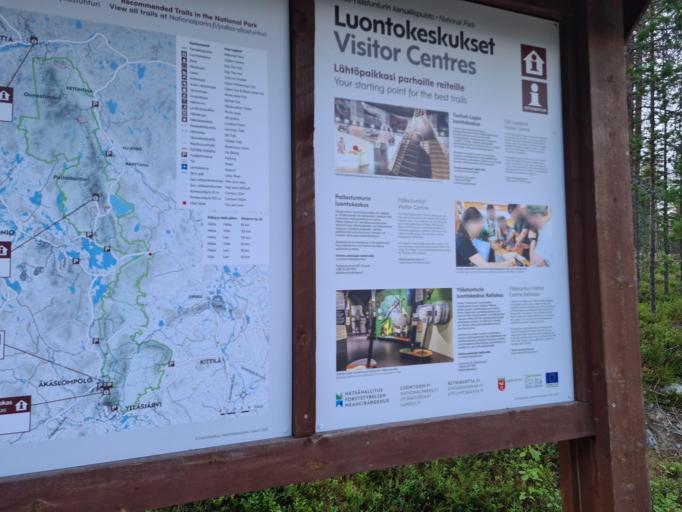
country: FI
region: Lapland
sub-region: Tunturi-Lappi
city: Kittilae
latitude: 67.9200
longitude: 24.4188
